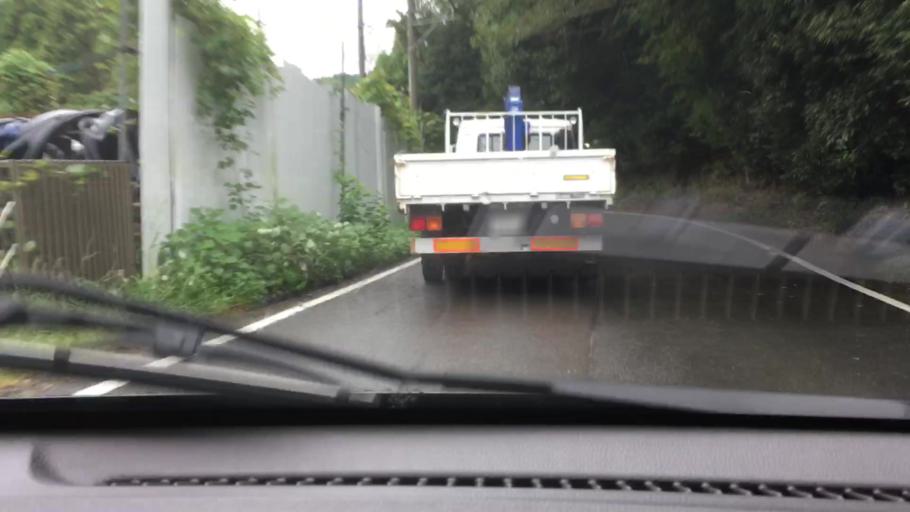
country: JP
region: Nagasaki
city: Togitsu
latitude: 32.8579
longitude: 129.7785
